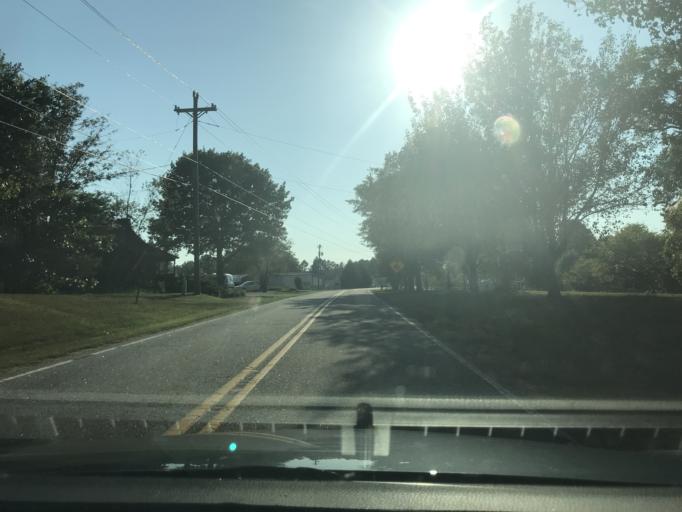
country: US
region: South Carolina
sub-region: Spartanburg County
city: Mayo
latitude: 35.1278
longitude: -81.7789
